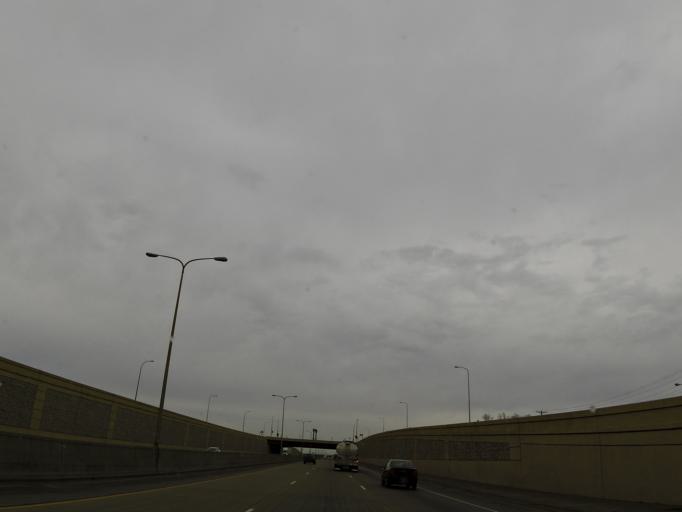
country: US
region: Minnesota
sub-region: Washington County
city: Newport
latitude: 44.8689
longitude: -92.9994
